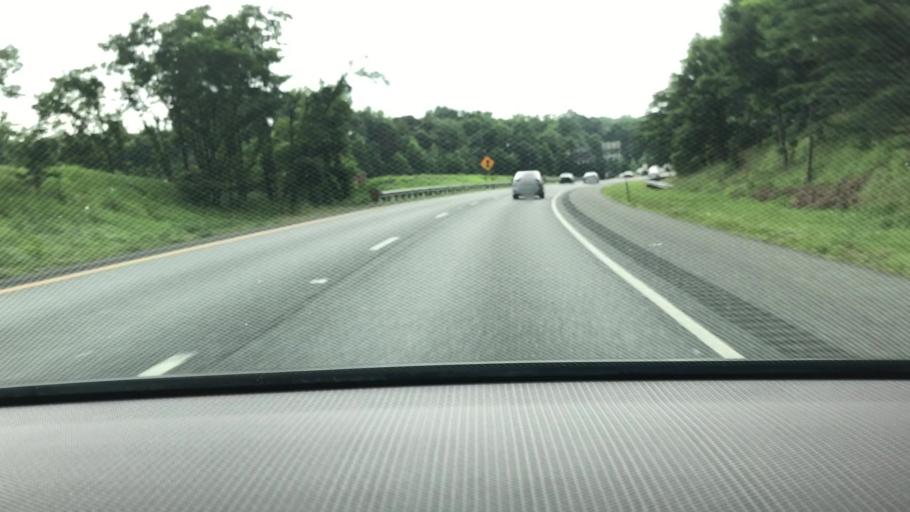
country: US
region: Maryland
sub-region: Anne Arundel County
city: Riva
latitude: 38.9862
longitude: -76.5764
